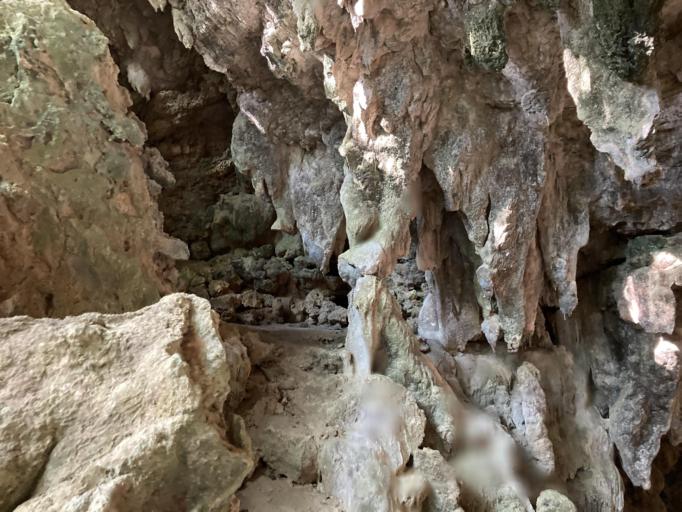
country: JP
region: Okinawa
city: Katsuren-haebaru
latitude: 26.3151
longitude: 127.9288
